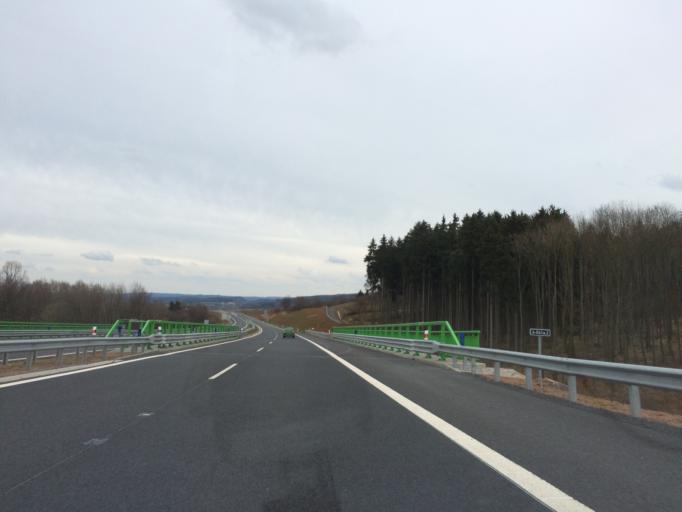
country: CZ
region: Ustecky
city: Lubenec
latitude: 50.1340
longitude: 13.2586
